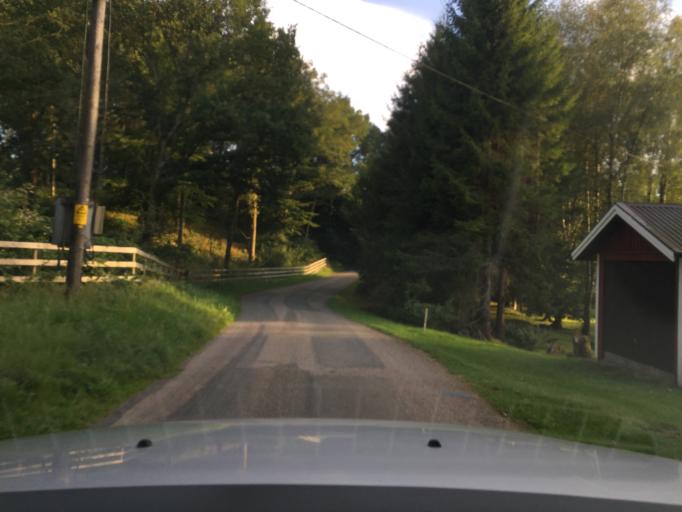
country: SE
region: Skane
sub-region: Hassleholms Kommun
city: Sosdala
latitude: 55.9924
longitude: 13.6054
